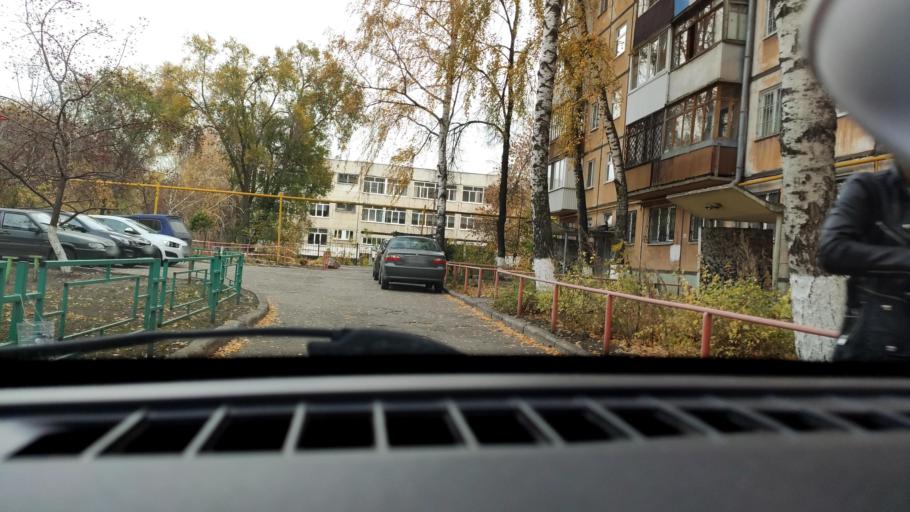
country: RU
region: Samara
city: Samara
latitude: 53.2265
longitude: 50.2058
